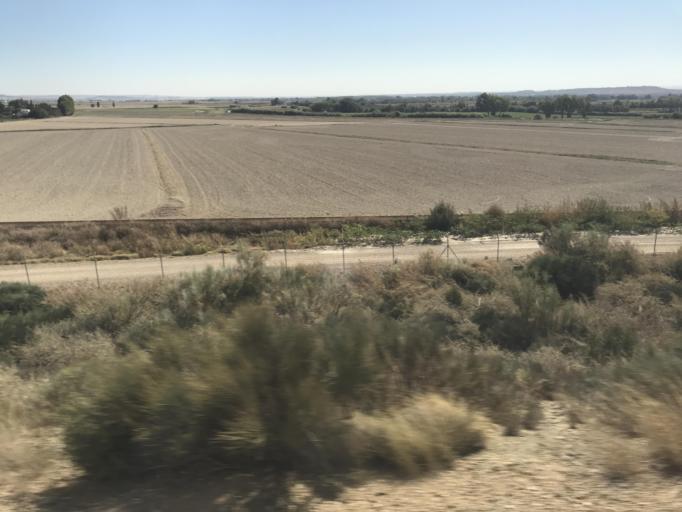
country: ES
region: Aragon
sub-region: Provincia de Zaragoza
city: Pina de Ebro
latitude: 41.5246
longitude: -0.5583
